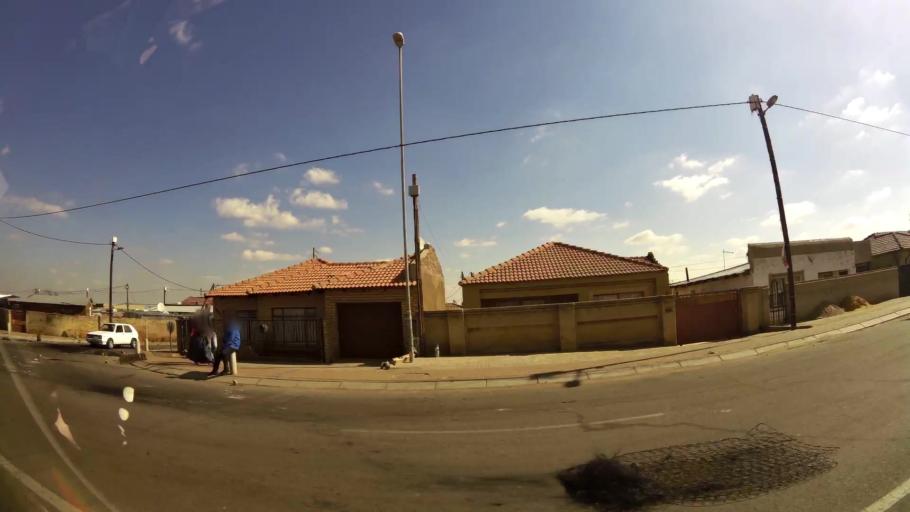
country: ZA
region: Gauteng
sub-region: West Rand District Municipality
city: Krugersdorp
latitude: -26.1567
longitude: 27.7841
